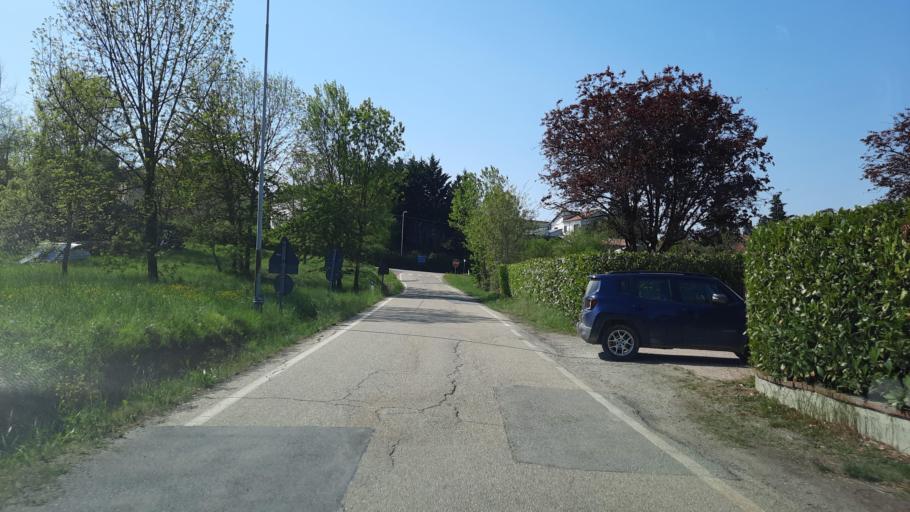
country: IT
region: Piedmont
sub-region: Provincia di Torino
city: Valentino
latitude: 45.1549
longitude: 8.0949
